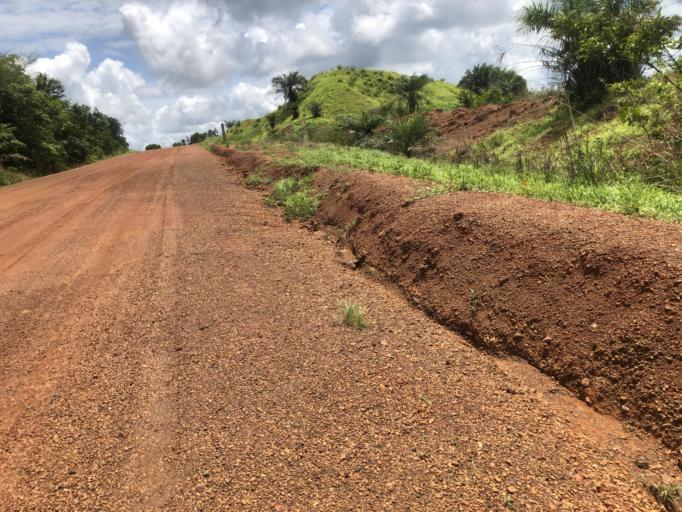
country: SL
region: Northern Province
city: Port Loko
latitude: 8.7184
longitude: -12.8462
